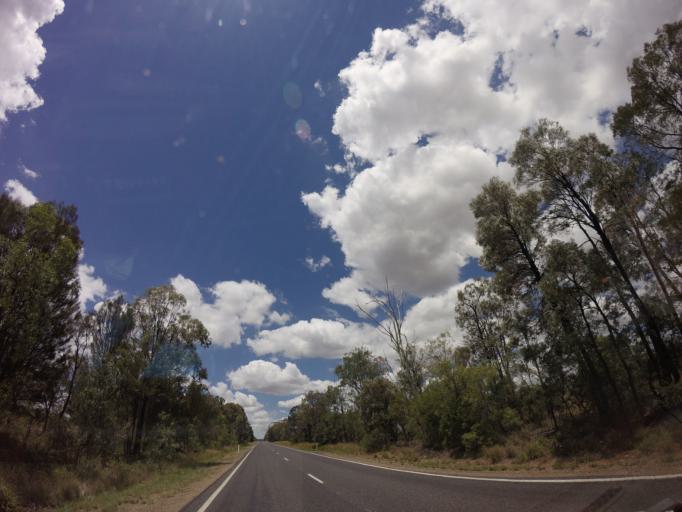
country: AU
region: Queensland
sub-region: Toowoomba
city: Oakey
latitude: -27.9473
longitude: 151.1469
